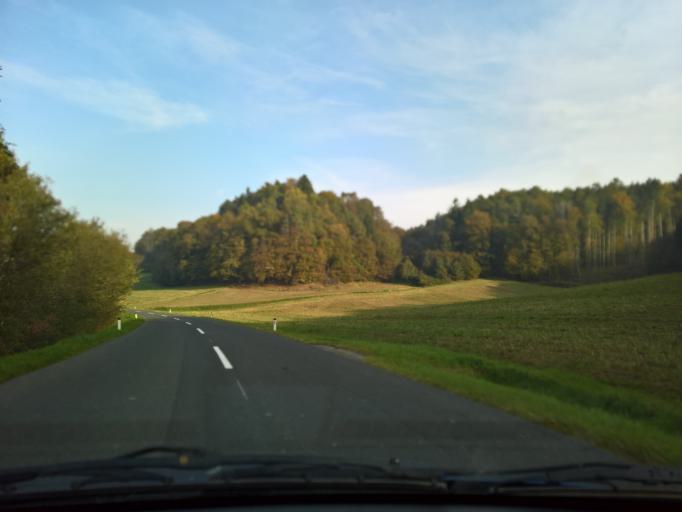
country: AT
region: Styria
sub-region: Politischer Bezirk Leibnitz
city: Pistorf
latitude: 46.7736
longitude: 15.3469
